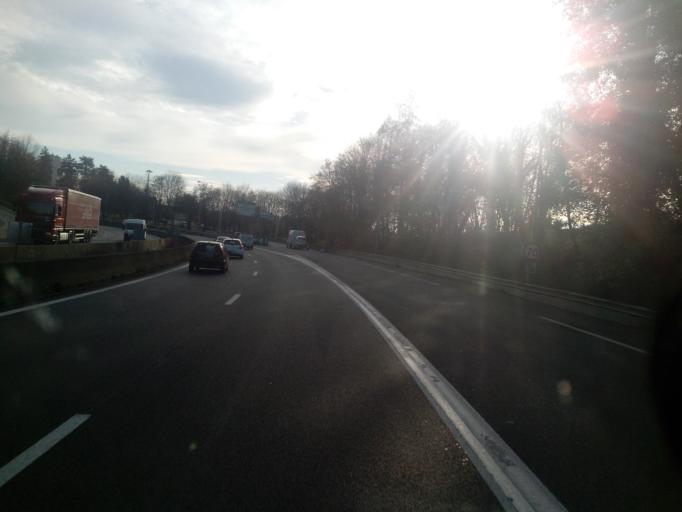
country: FR
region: Limousin
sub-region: Departement de la Haute-Vienne
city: Limoges
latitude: 45.8309
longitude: 1.2822
